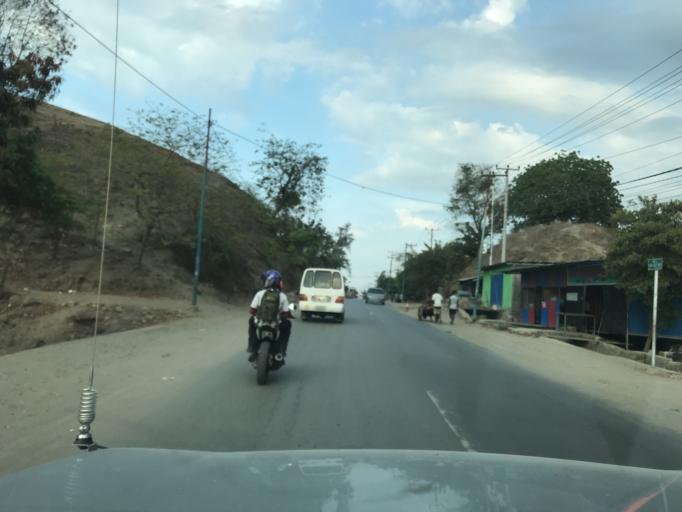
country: TL
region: Dili
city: Dili
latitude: -8.5545
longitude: 125.5156
